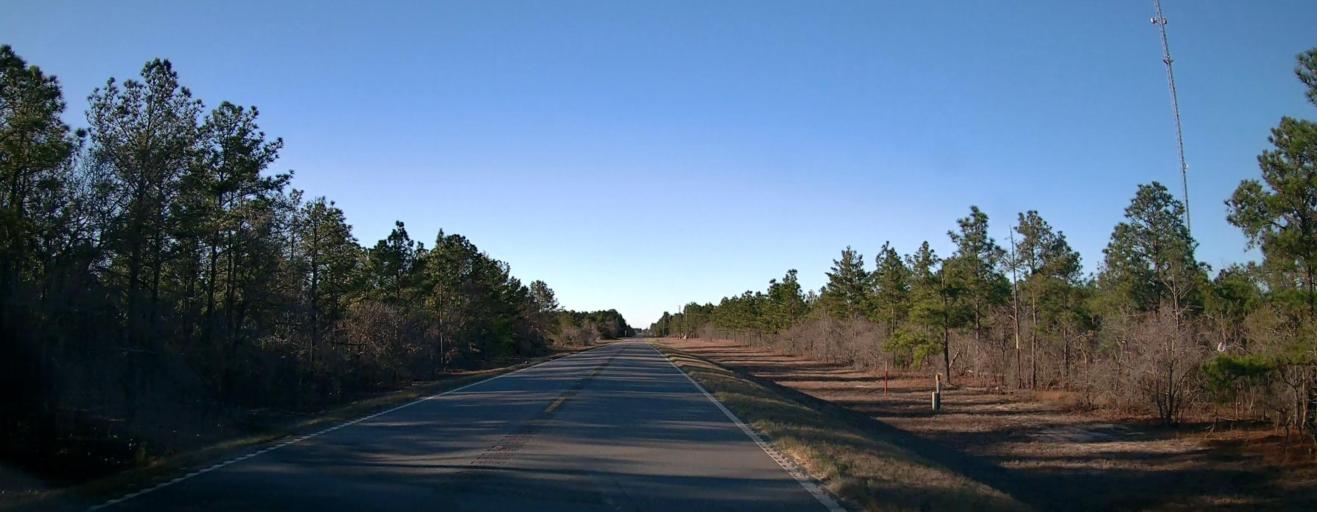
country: US
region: Georgia
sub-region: Talbot County
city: Talbotton
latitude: 32.5699
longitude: -84.4408
